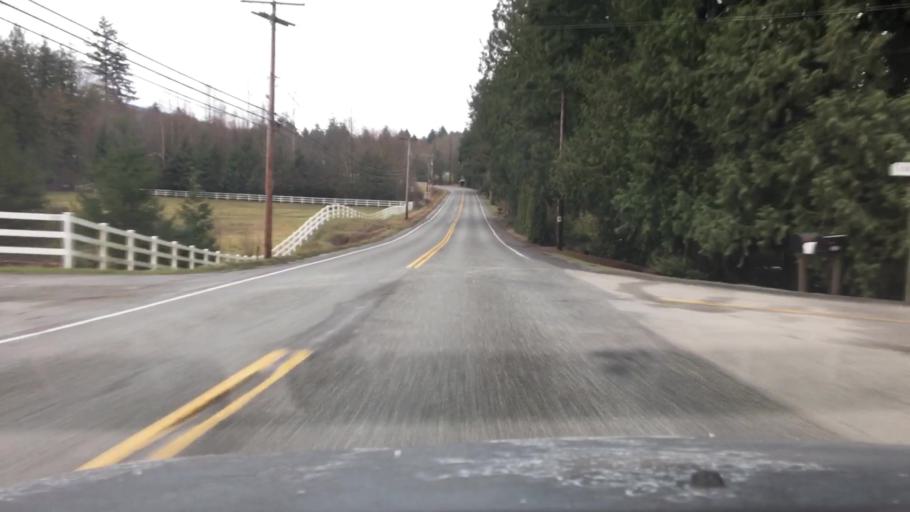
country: US
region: Washington
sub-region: Whatcom County
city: Sudden Valley
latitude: 48.6495
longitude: -122.3243
